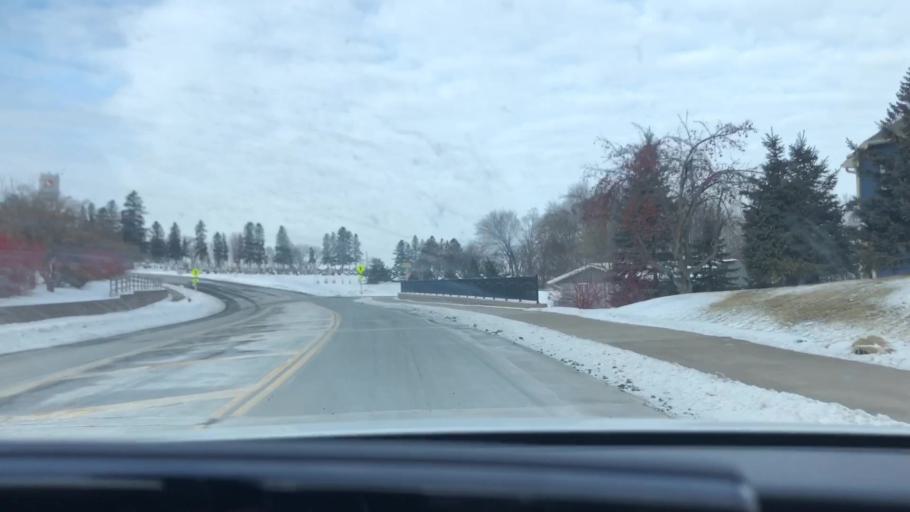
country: US
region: Minnesota
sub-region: Carver County
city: Waconia
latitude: 44.8501
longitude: -93.7743
